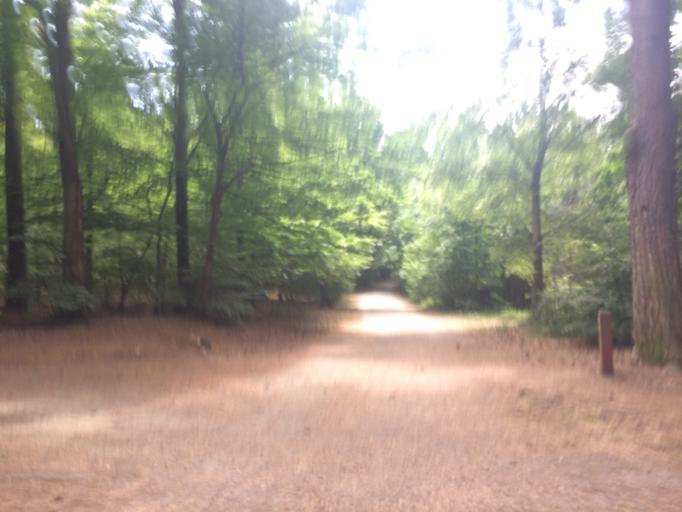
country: DK
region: Capital Region
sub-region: Bornholm Kommune
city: Ronne
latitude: 55.1313
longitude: 14.7149
